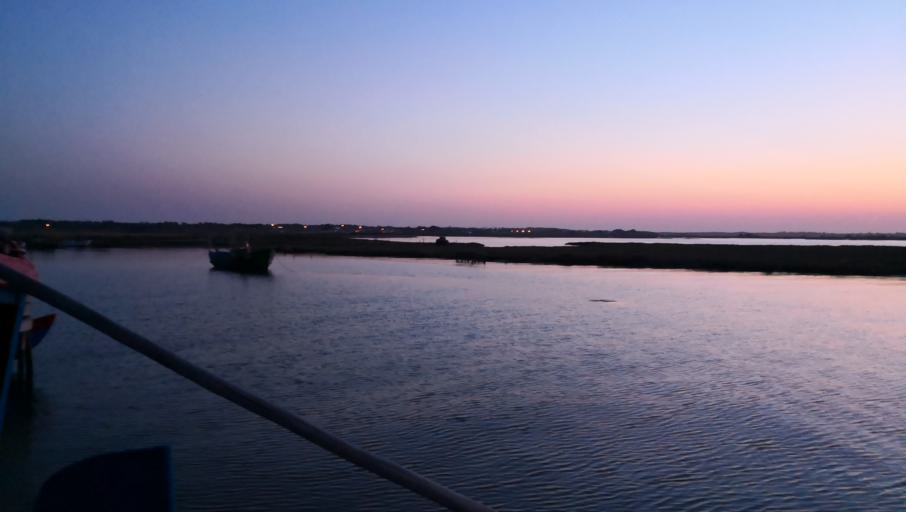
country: PT
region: Setubal
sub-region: Setubal
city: Setubal
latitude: 38.4136
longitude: -8.7576
